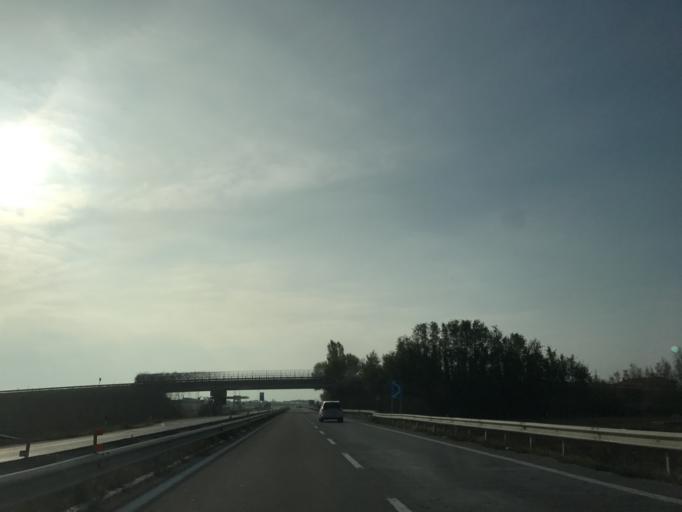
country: IT
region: Emilia-Romagna
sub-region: Provincia di Rimini
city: Bellaria-Igea Marina
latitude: 44.1207
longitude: 12.4730
